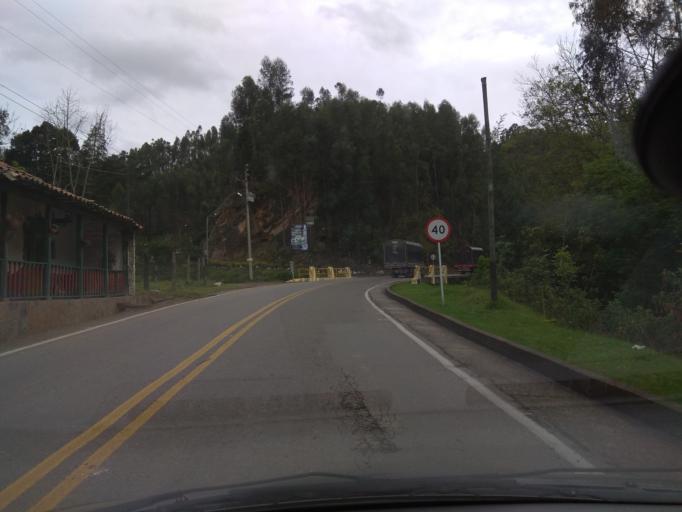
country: CO
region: Boyaca
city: Duitama
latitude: 5.8472
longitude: -73.0146
